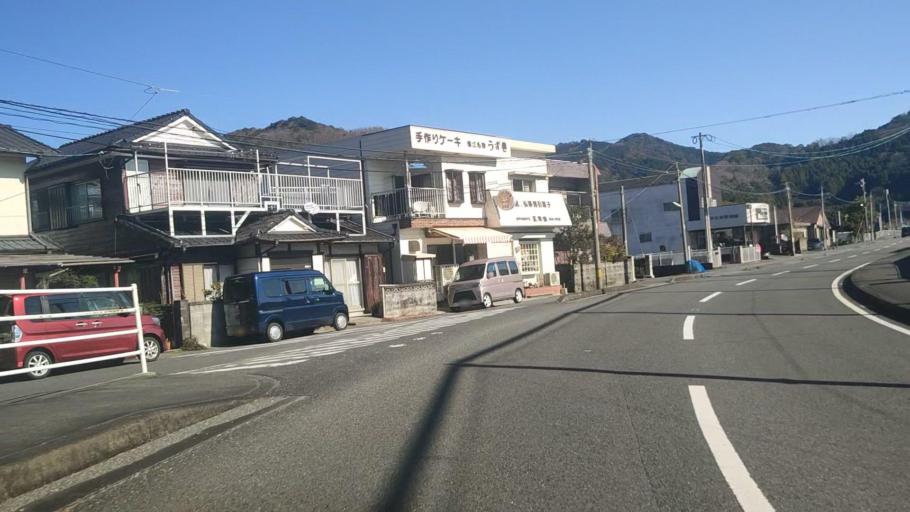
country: JP
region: Oita
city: Saiki
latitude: 32.8013
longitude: 131.9204
